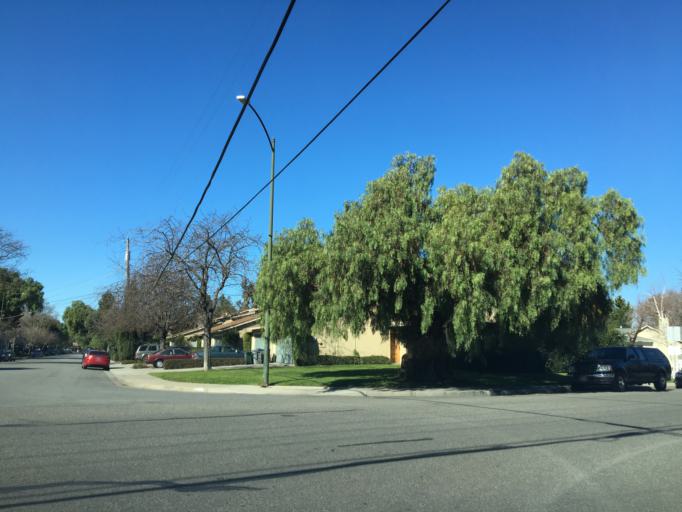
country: US
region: California
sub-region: Santa Clara County
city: Mountain View
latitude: 37.4094
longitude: -122.0888
